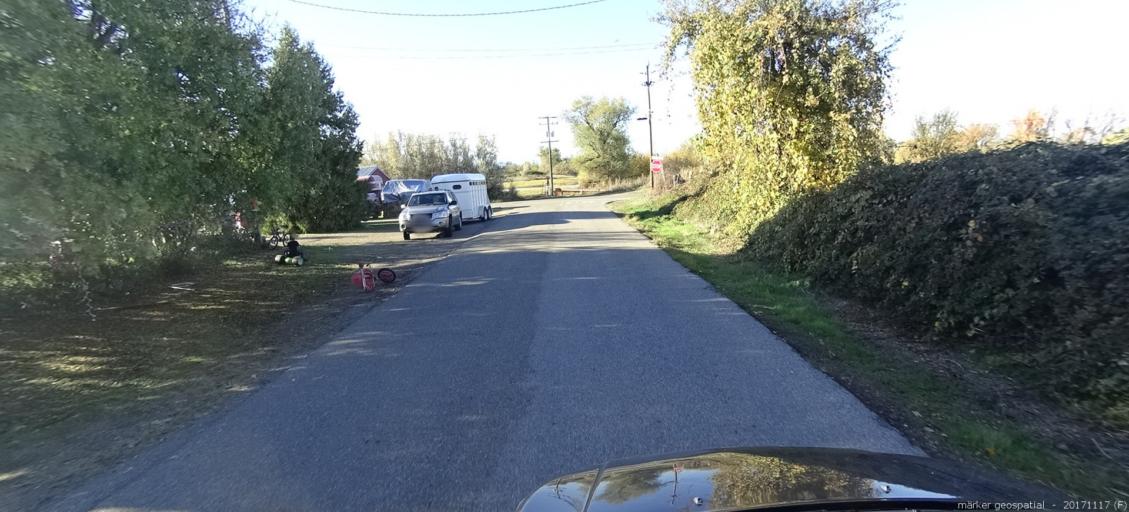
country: US
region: California
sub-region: Shasta County
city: Cottonwood
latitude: 40.4207
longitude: -122.2314
